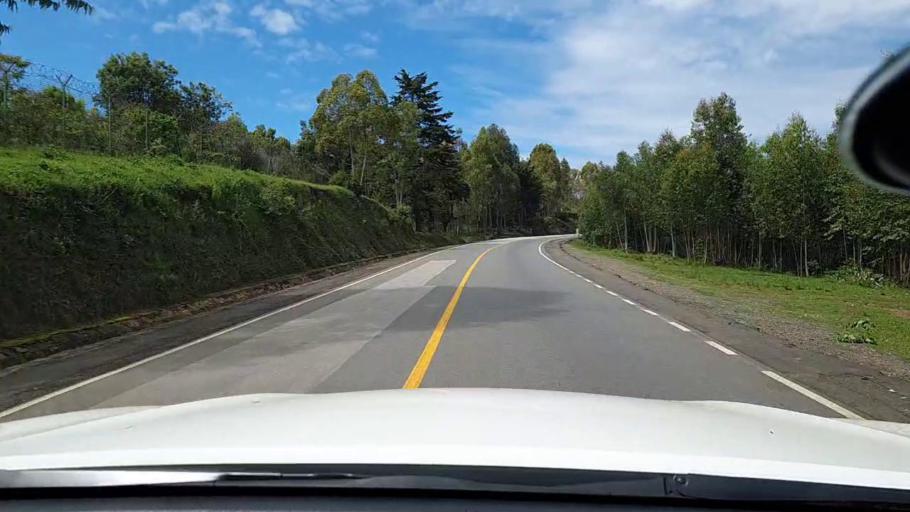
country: RW
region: Kigali
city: Kigali
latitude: -1.8238
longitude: 29.9473
